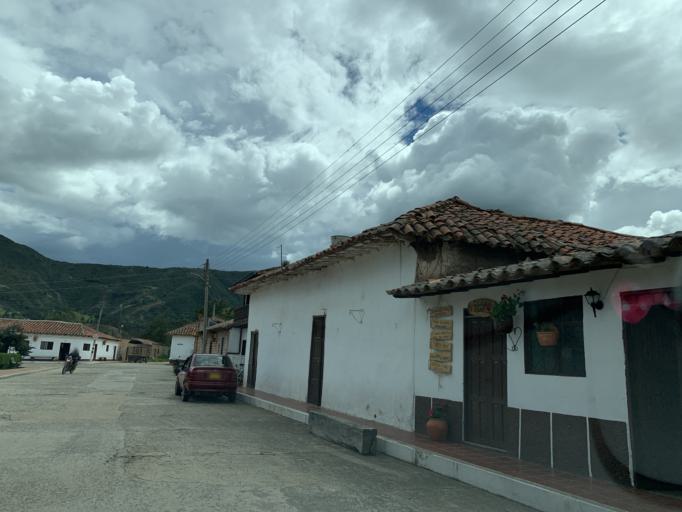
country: CO
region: Boyaca
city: Floresta
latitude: 5.8569
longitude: -72.9439
